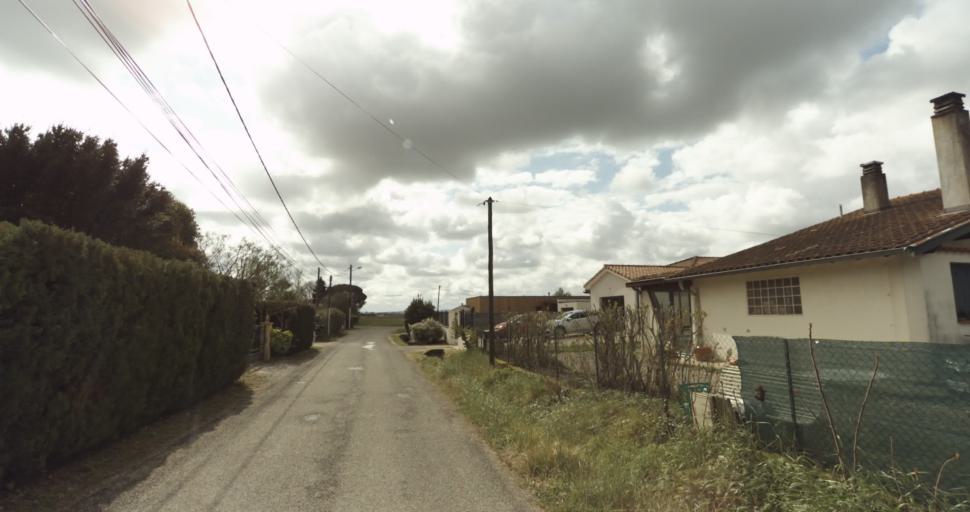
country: FR
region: Midi-Pyrenees
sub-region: Departement de la Haute-Garonne
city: Auterive
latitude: 43.3416
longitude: 1.4666
